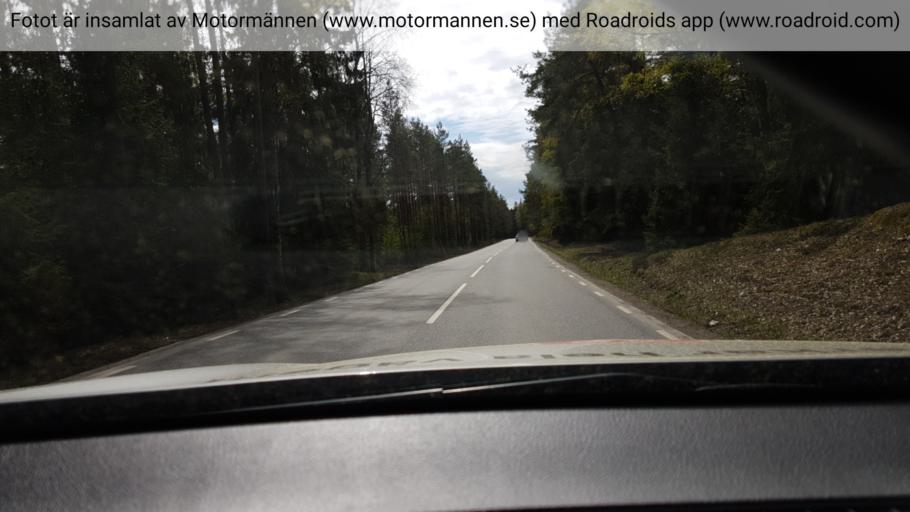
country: SE
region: Stockholm
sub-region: Haninge Kommun
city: Haninge
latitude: 59.1620
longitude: 18.1821
